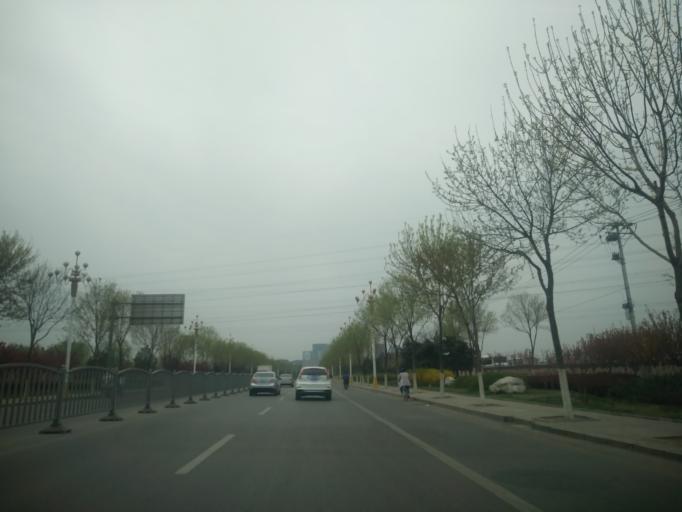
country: CN
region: Beijing
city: Jiugong
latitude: 39.8072
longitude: 116.4645
